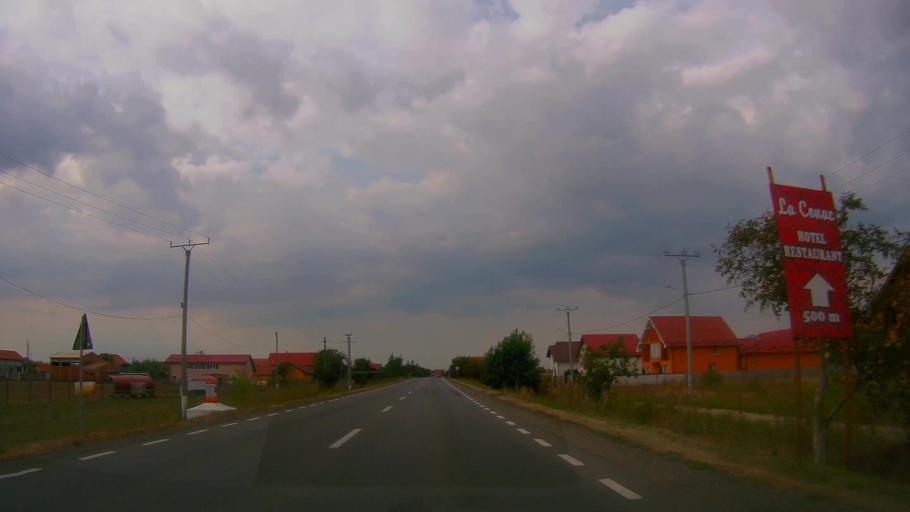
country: RO
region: Satu Mare
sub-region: Comuna Botiz
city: Botiz
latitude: 47.8379
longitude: 22.9592
